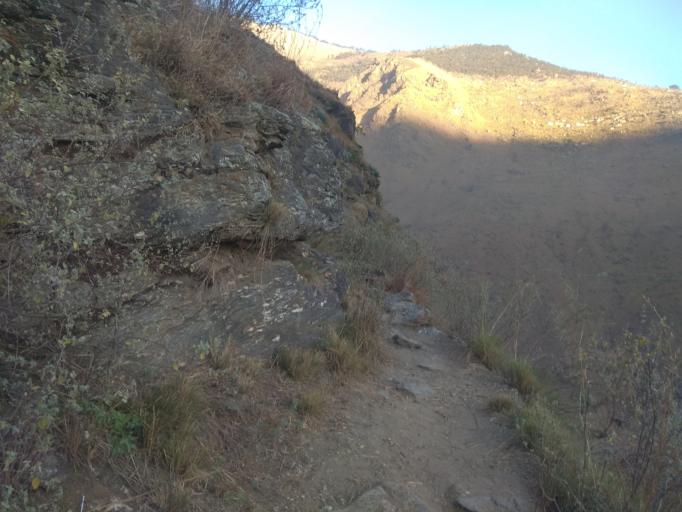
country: NP
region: Mid Western
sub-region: Bheri Zone
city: Dailekh
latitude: 29.2851
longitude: 81.7177
